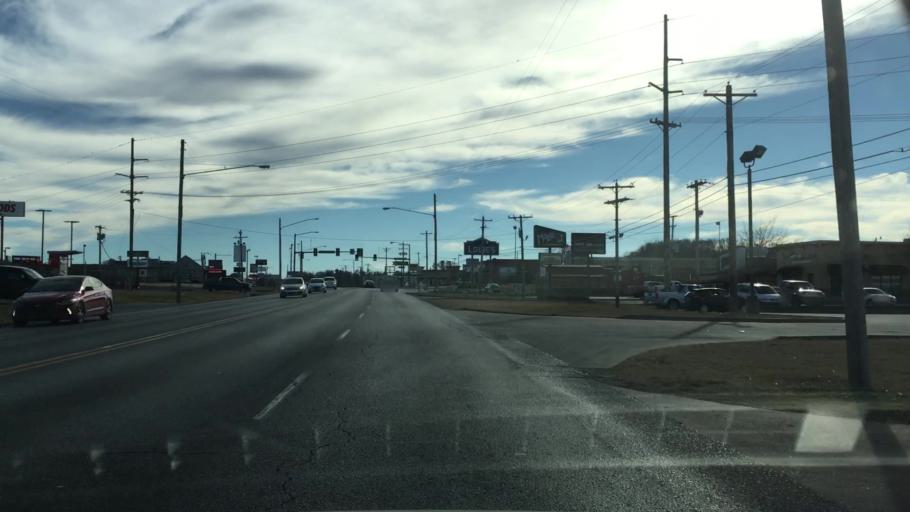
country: US
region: Oklahoma
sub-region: Cherokee County
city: Tahlequah
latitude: 35.8945
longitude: -94.9771
